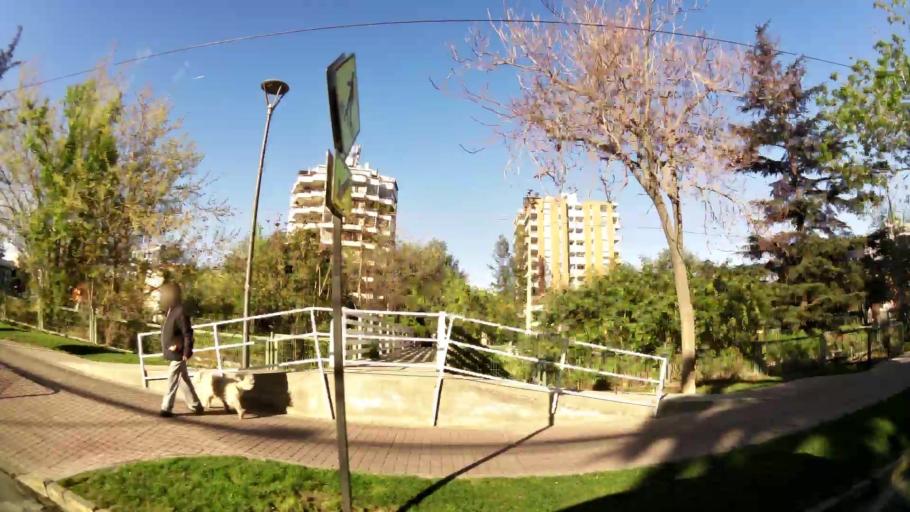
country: CL
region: Santiago Metropolitan
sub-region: Provincia de Santiago
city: Villa Presidente Frei, Nunoa, Santiago, Chile
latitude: -33.4254
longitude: -70.5916
